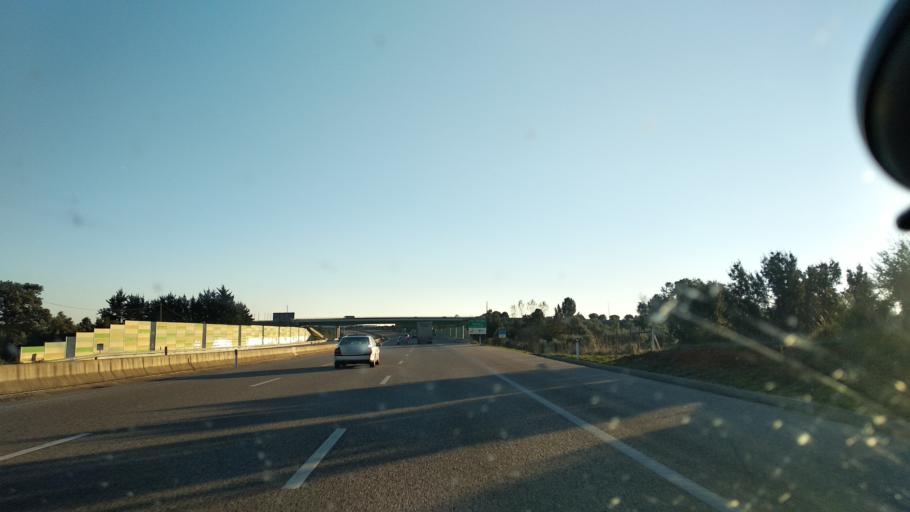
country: PT
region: Santarem
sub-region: Alcanena
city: Alcanena
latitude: 39.4586
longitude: -8.6306
